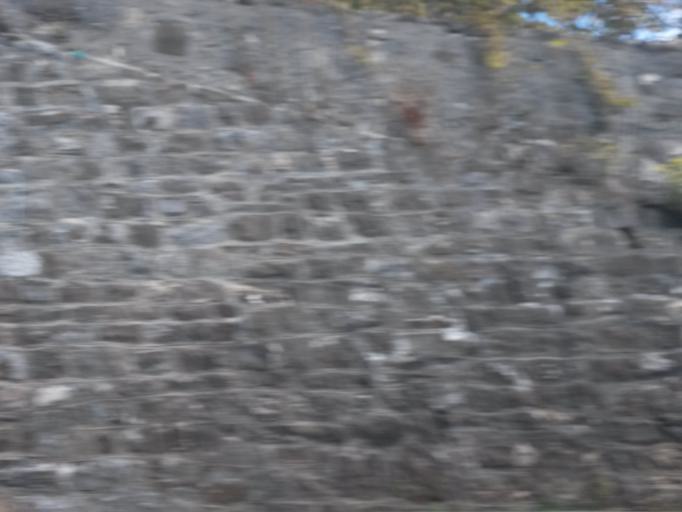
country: CH
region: Vaud
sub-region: Lavaux-Oron District
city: Cully
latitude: 46.4918
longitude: 6.7130
